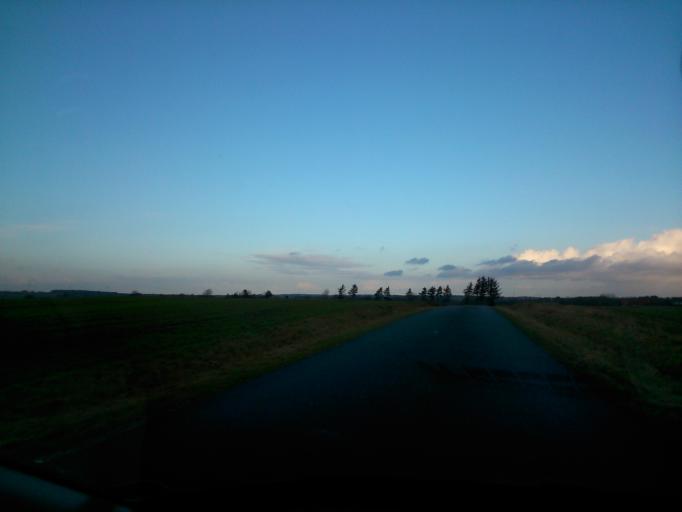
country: DK
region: Central Jutland
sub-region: Ringkobing-Skjern Kommune
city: Videbaek
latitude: 56.0425
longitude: 8.5677
